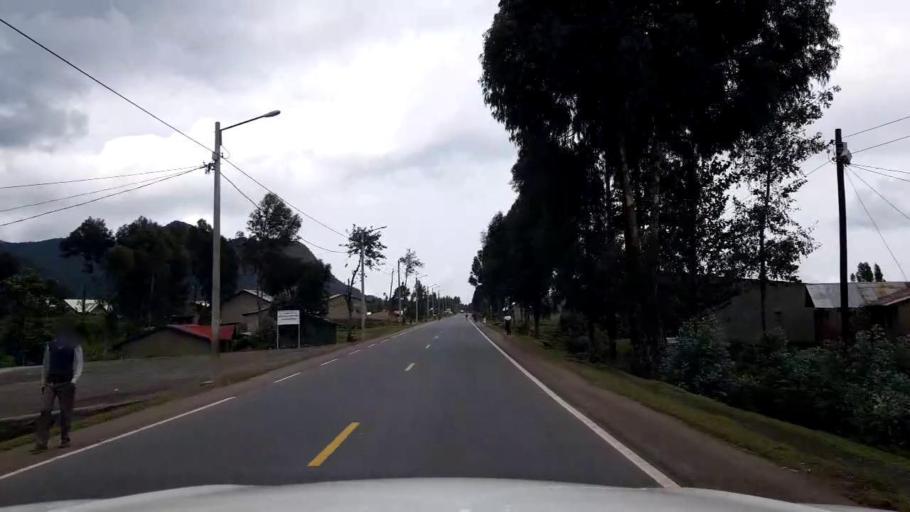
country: RW
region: Western Province
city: Gisenyi
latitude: -1.6347
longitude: 29.4099
